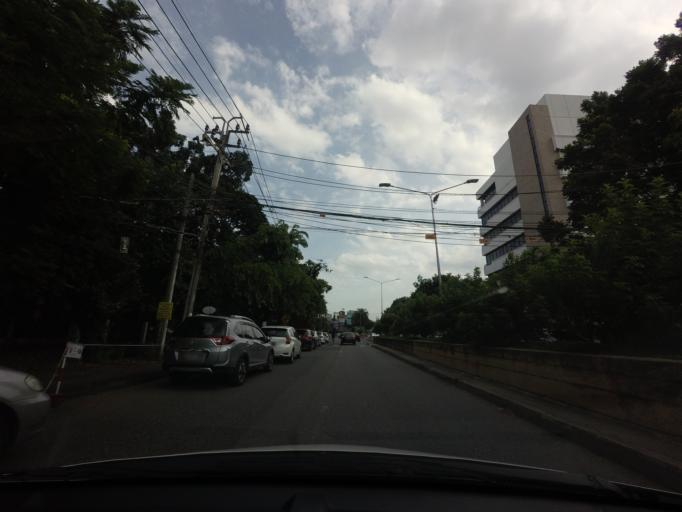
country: TH
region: Bangkok
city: Chatuchak
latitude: 13.8431
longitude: 100.5720
